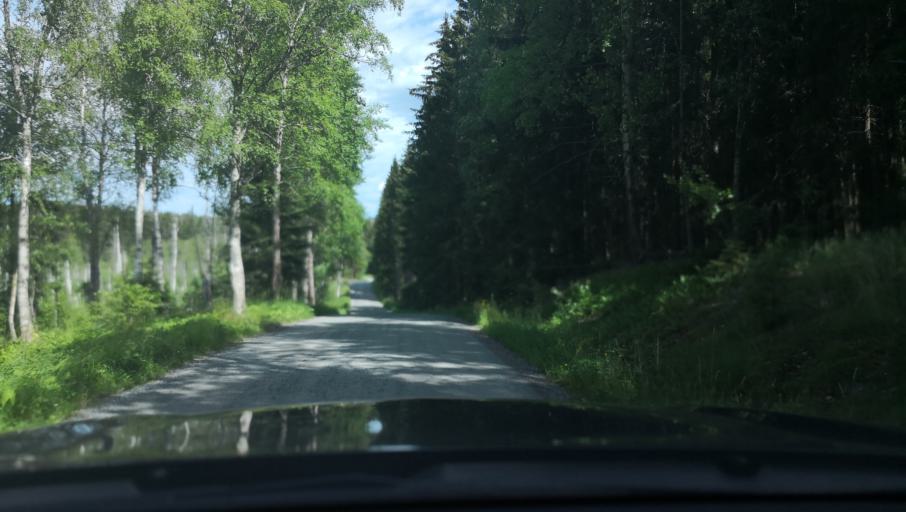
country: SE
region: Vaestmanland
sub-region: Surahammars Kommun
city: Ramnas
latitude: 59.8779
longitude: 16.0889
